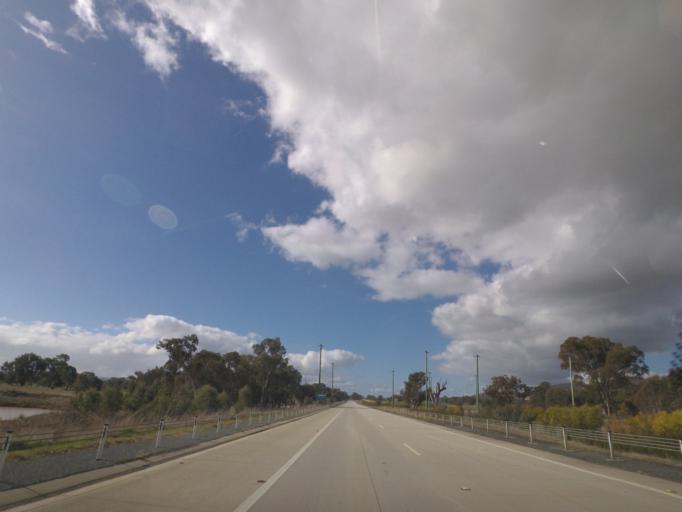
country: AU
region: New South Wales
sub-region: Greater Hume Shire
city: Holbrook
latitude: -35.6964
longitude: 147.3398
